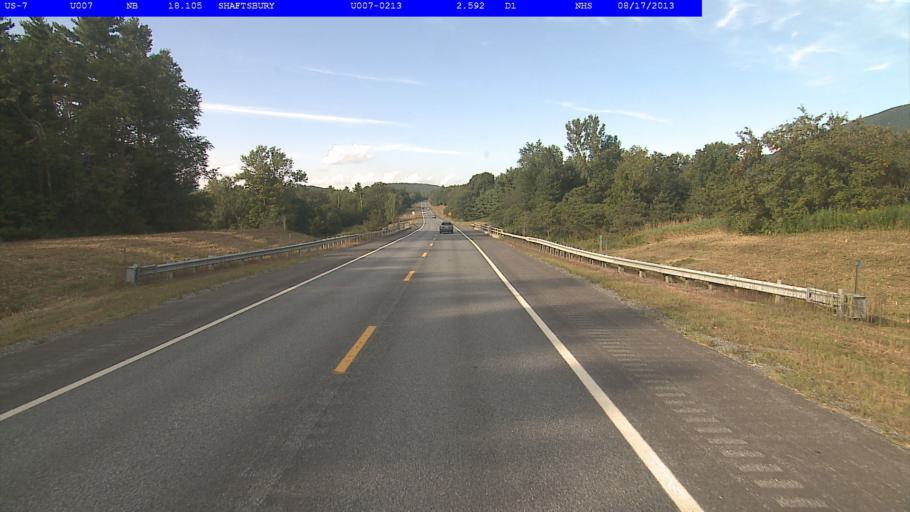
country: US
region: Vermont
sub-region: Bennington County
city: North Bennington
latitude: 42.9652
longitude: -73.1642
